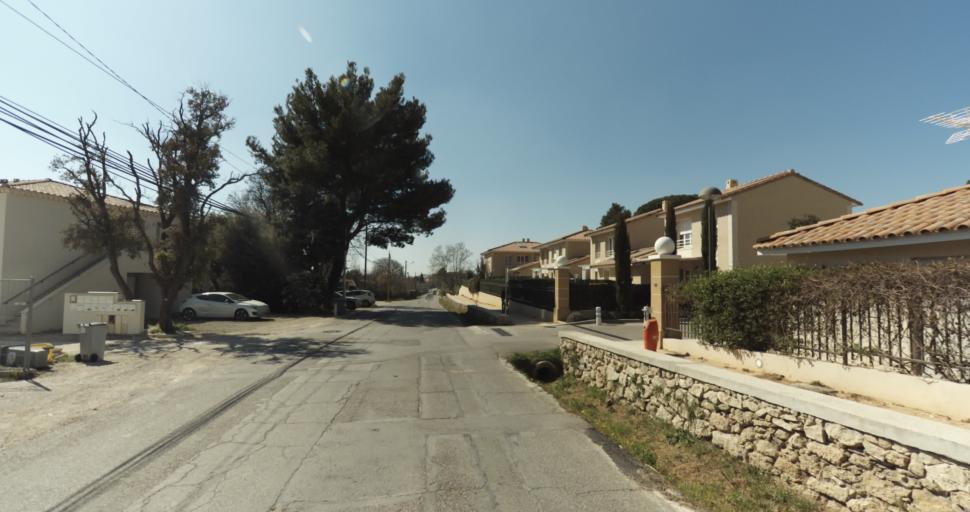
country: FR
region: Provence-Alpes-Cote d'Azur
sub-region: Departement des Bouches-du-Rhone
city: Pelissanne
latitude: 43.6346
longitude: 5.1631
